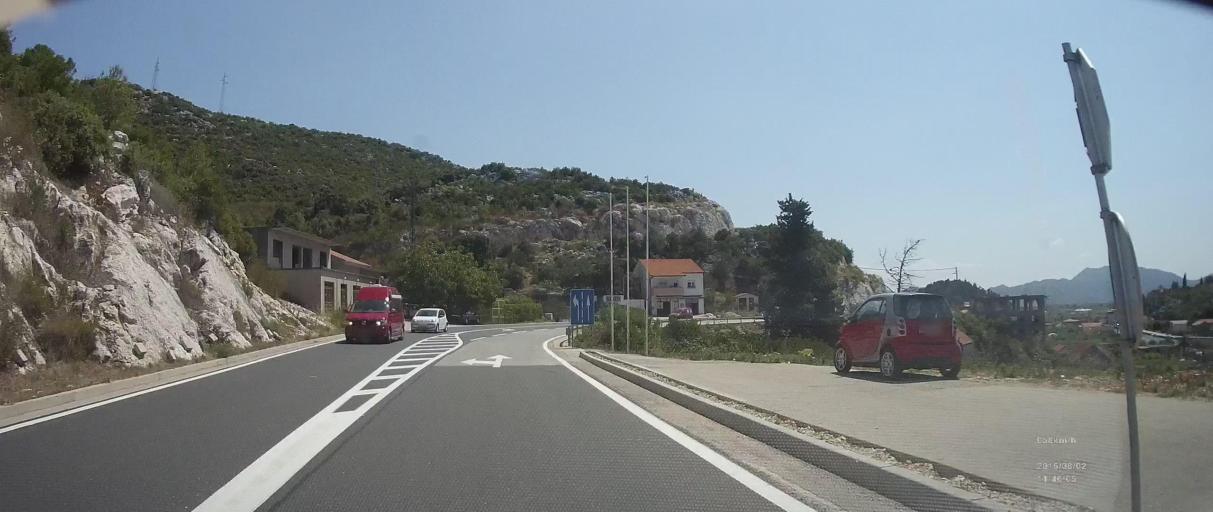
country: HR
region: Dubrovacko-Neretvanska
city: Komin
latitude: 43.0534
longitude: 17.4726
